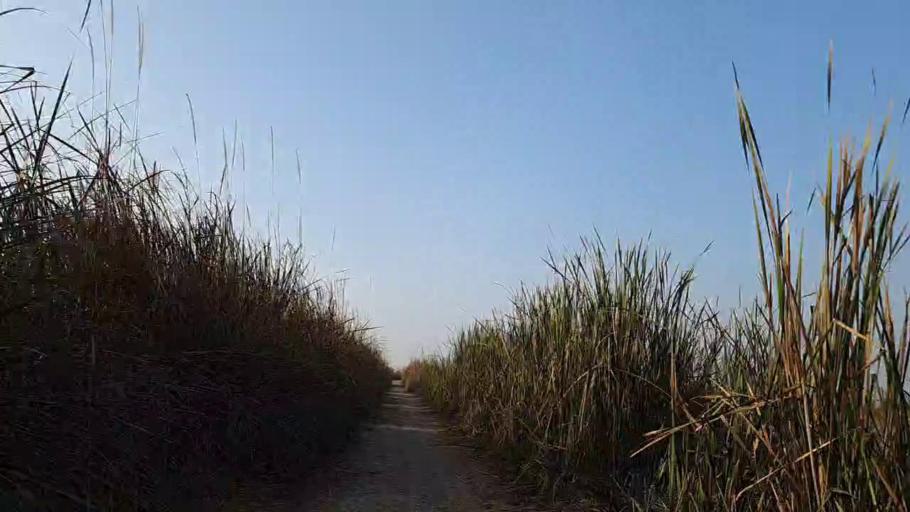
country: PK
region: Sindh
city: Sakrand
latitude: 26.0923
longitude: 68.3803
